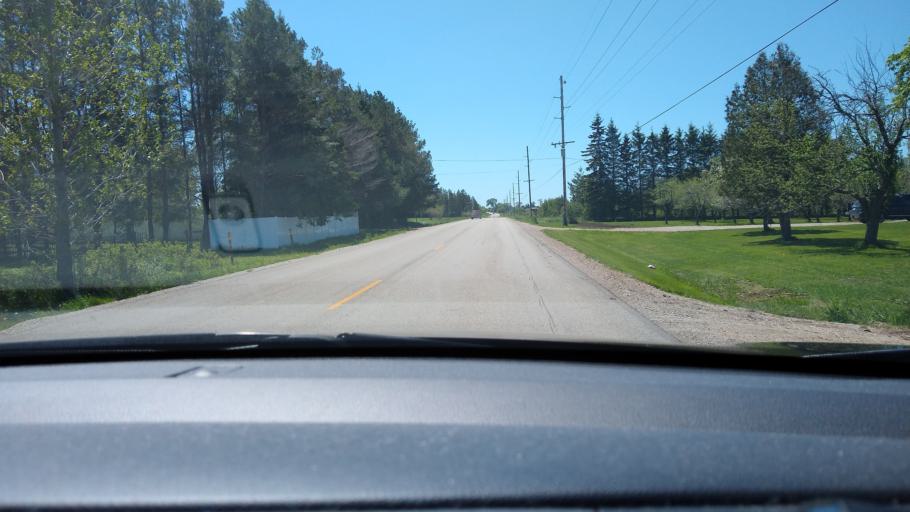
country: US
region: Michigan
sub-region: Delta County
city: Escanaba
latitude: 45.8490
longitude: -87.1843
